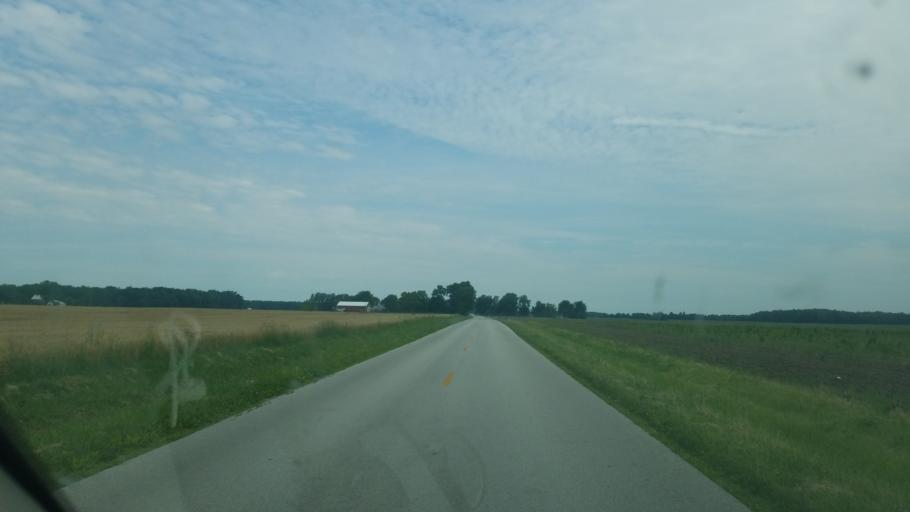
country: US
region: Ohio
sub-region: Wyandot County
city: Carey
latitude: 41.0453
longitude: -83.4392
